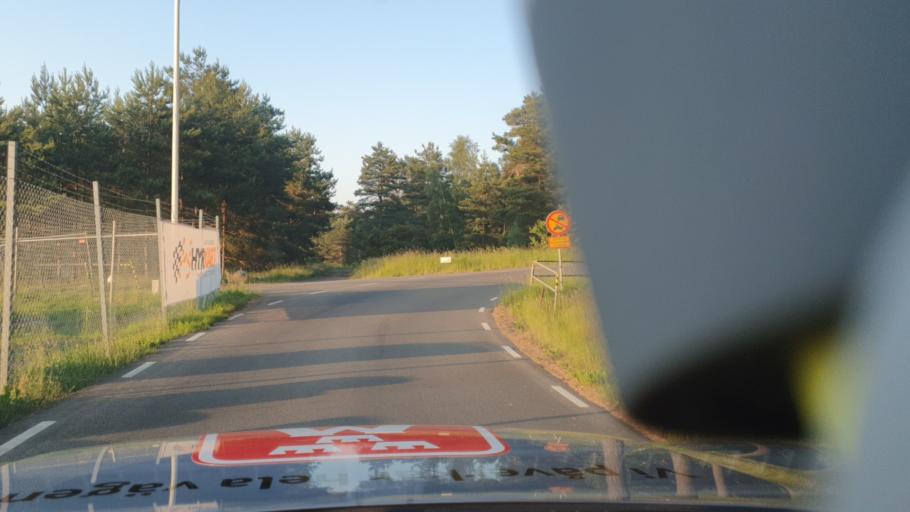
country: SE
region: Skane
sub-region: Kristianstads Kommun
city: Norra Asum
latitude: 55.9869
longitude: 14.1253
